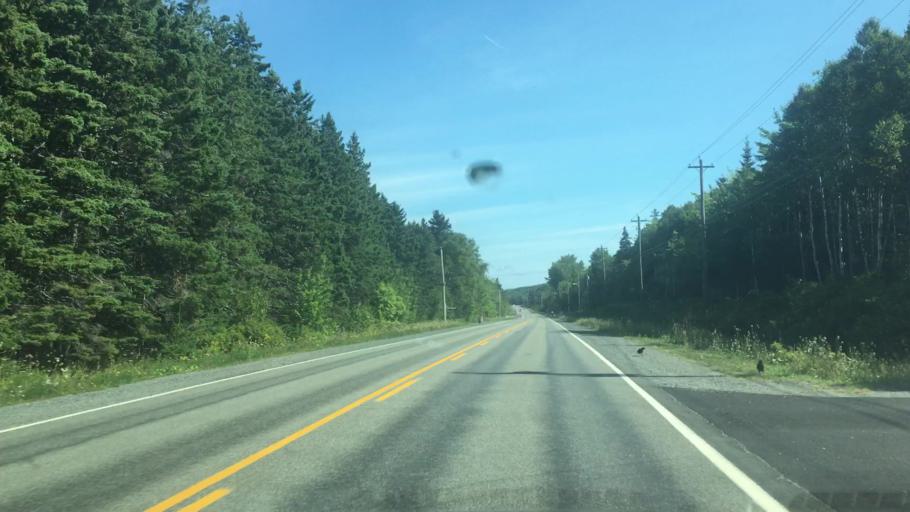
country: CA
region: Nova Scotia
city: Sydney
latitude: 45.9818
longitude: -60.4255
